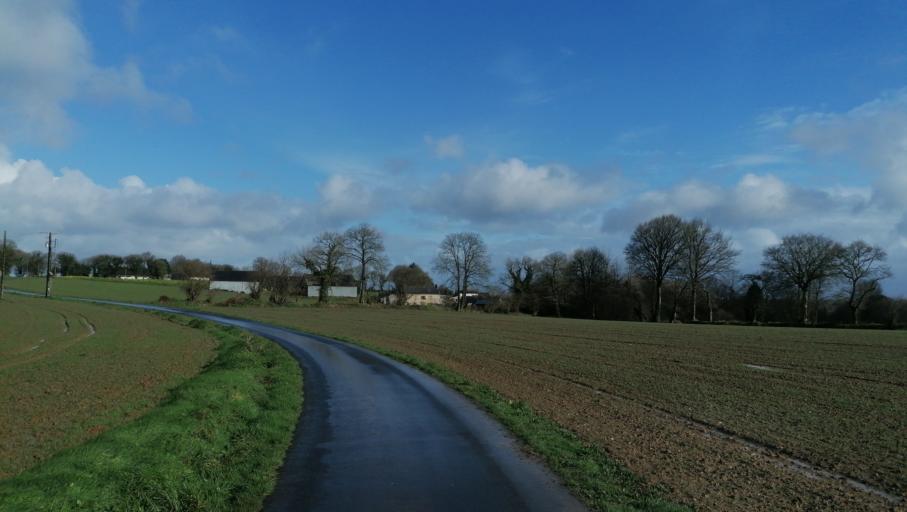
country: FR
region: Brittany
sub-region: Departement des Cotes-d'Armor
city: Lanrodec
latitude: 48.4837
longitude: -3.0196
